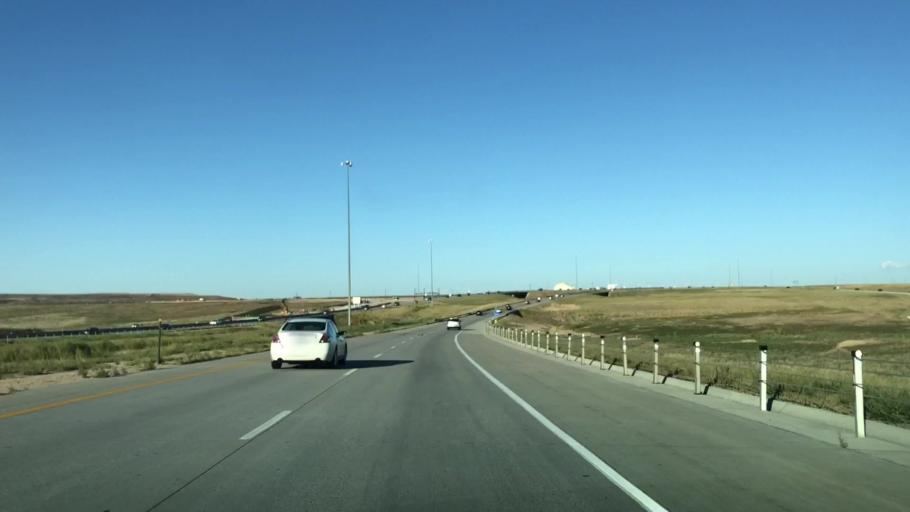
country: US
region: Colorado
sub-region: Adams County
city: Aurora
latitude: 39.8307
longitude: -104.7792
